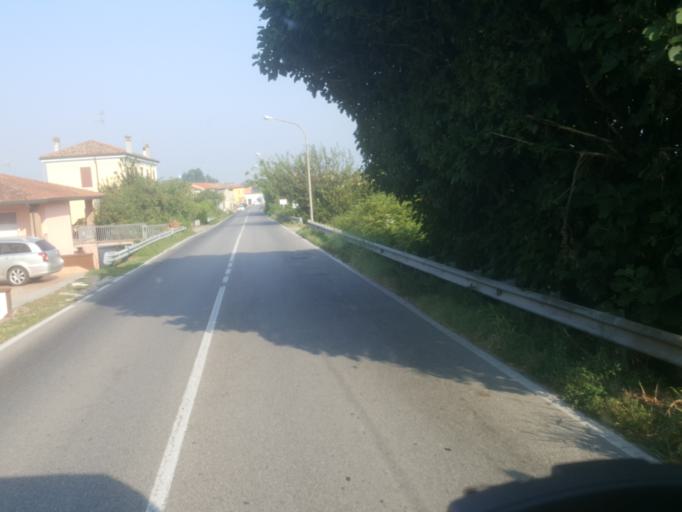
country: IT
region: Emilia-Romagna
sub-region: Provincia di Ravenna
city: Glorie
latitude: 44.4704
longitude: 12.0820
